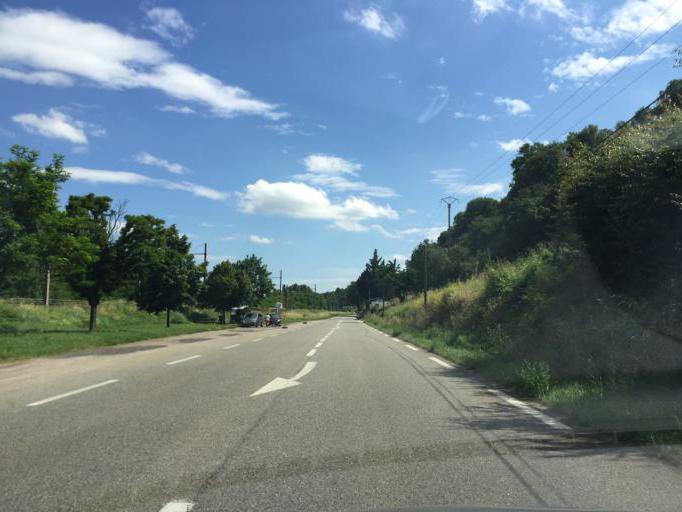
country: FR
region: Rhone-Alpes
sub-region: Departement de l'Ardeche
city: Andance
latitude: 45.2328
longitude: 4.7997
